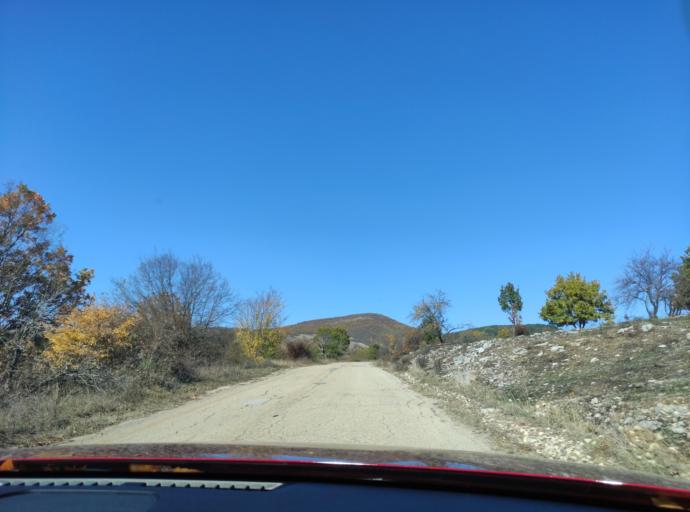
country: BG
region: Montana
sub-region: Obshtina Chiprovtsi
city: Chiprovtsi
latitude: 43.4449
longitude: 23.0482
